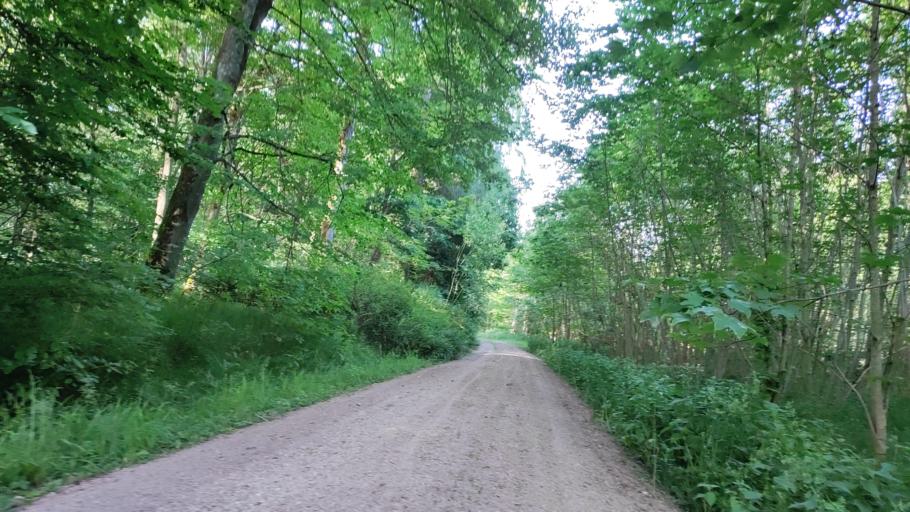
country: DE
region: Bavaria
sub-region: Swabia
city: Rosshaupten
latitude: 48.4163
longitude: 10.4950
